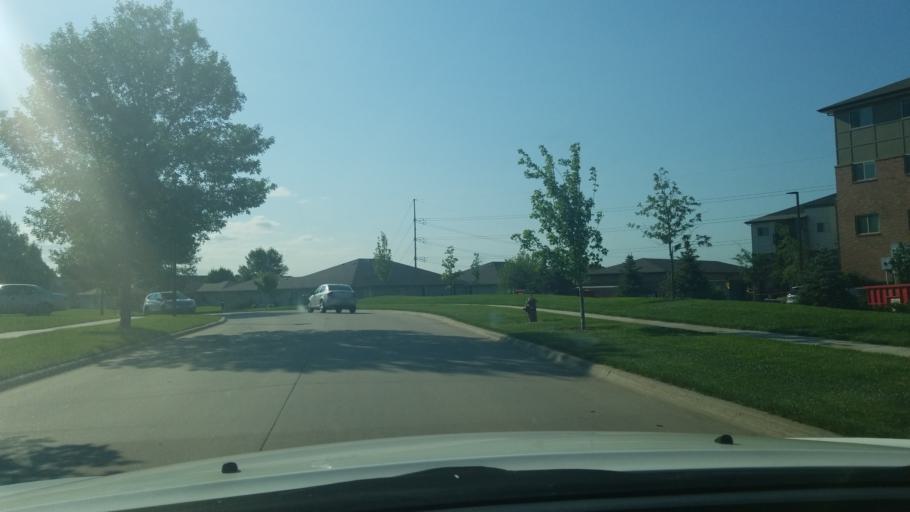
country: US
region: Nebraska
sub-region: Lancaster County
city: Lincoln
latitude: 40.7502
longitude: -96.6089
